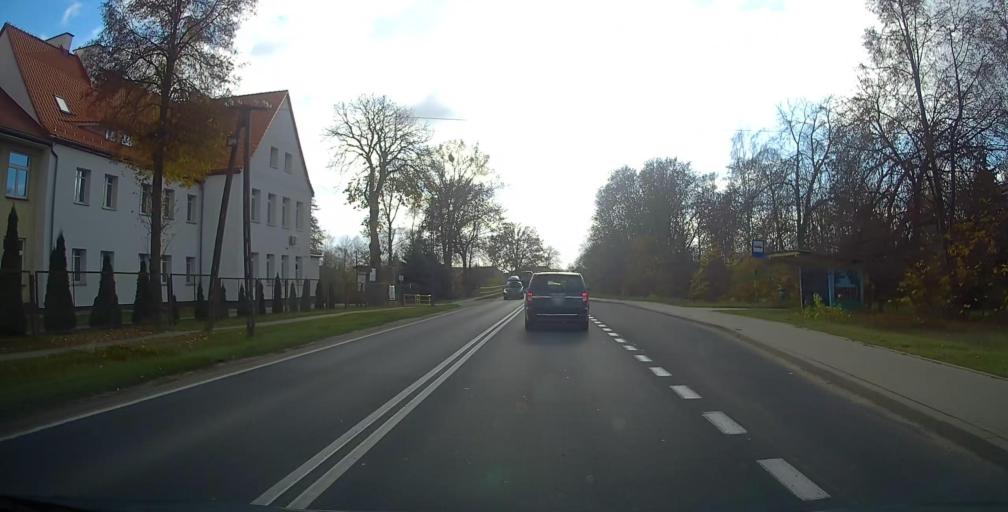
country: PL
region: Warmian-Masurian Voivodeship
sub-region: Powiat elcki
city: Elk
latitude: 53.7698
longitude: 22.3357
